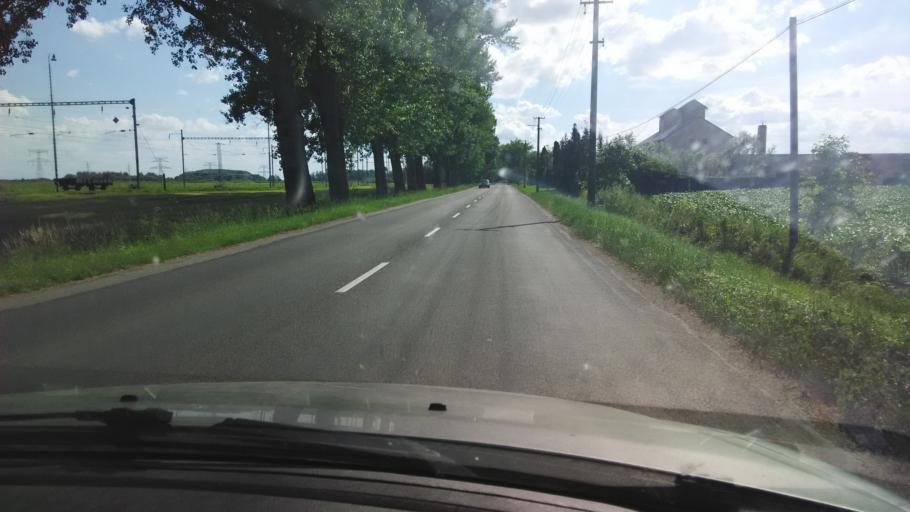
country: SK
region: Nitriansky
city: Surany
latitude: 48.0974
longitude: 18.2308
